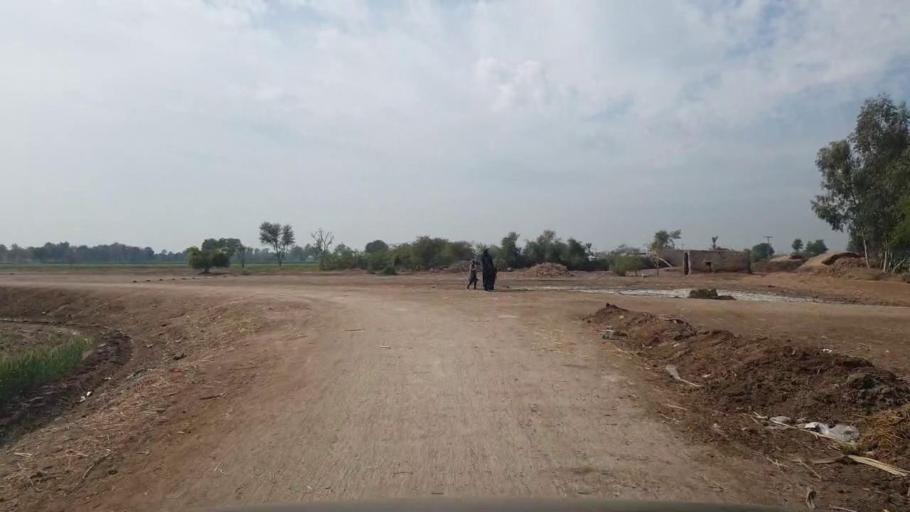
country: PK
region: Sindh
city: Sakrand
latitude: 25.9974
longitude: 68.3802
